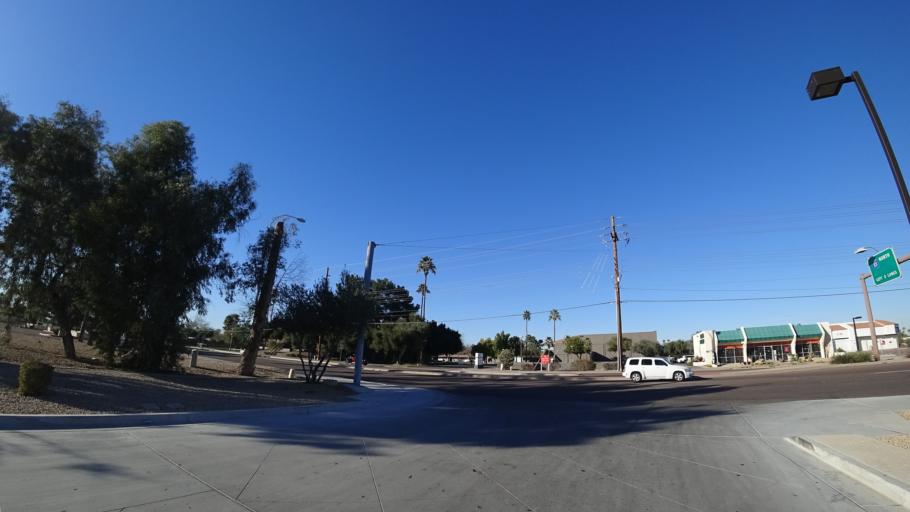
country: US
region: Arizona
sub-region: Maricopa County
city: Tempe
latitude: 33.3926
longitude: -111.8931
